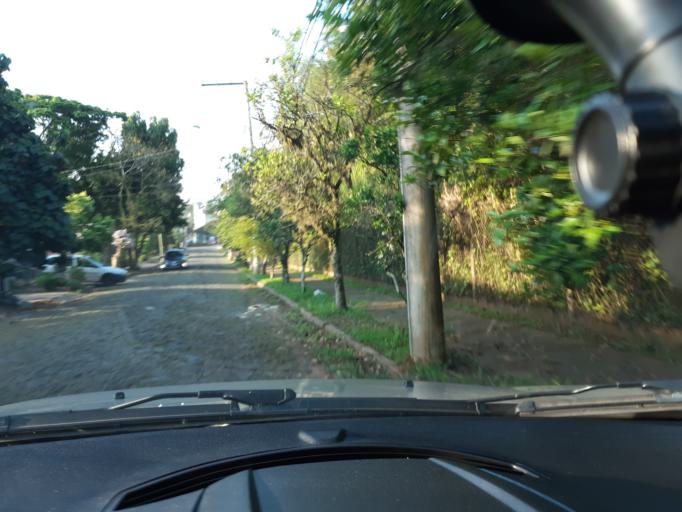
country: BR
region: Rio Grande do Sul
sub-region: Sao Leopoldo
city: Sao Leopoldo
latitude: -29.7744
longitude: -51.1401
